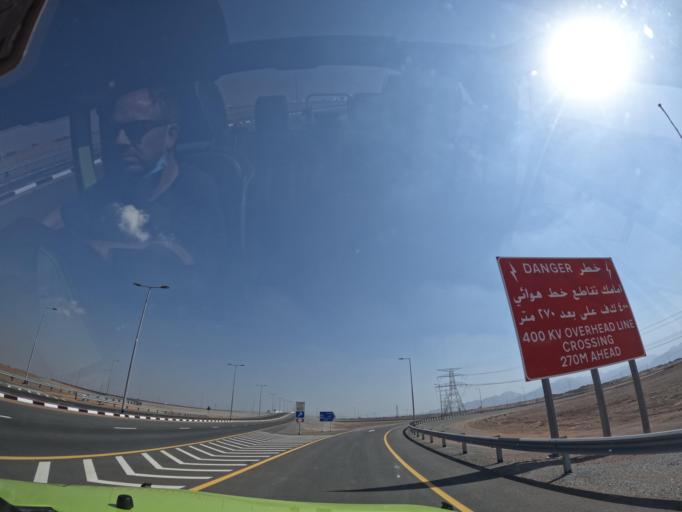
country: AE
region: Ash Shariqah
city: Adh Dhayd
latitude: 24.8125
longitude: 55.7993
